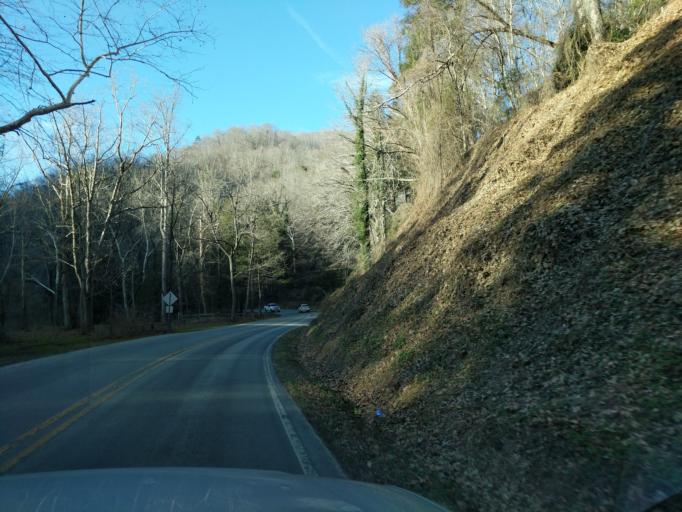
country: US
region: North Carolina
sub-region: Henderson County
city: Edneyville
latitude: 35.4560
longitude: -82.2975
